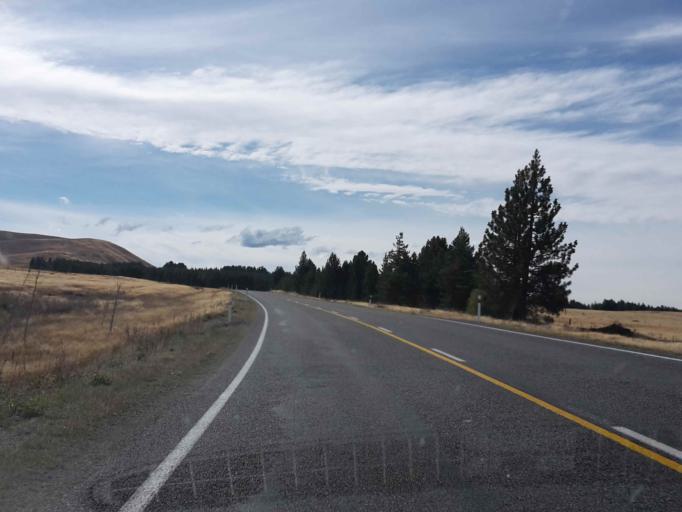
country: NZ
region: Canterbury
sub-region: Timaru District
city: Pleasant Point
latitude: -44.0196
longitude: 170.4032
